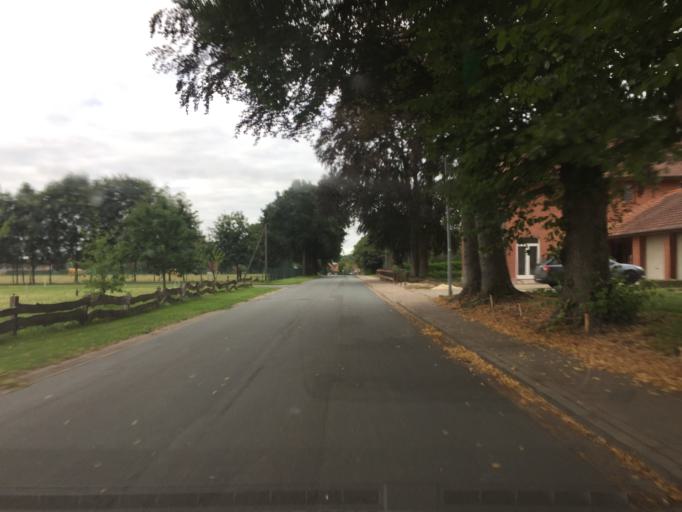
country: DE
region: Lower Saxony
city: Ehrenburg
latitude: 52.7501
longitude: 8.7134
